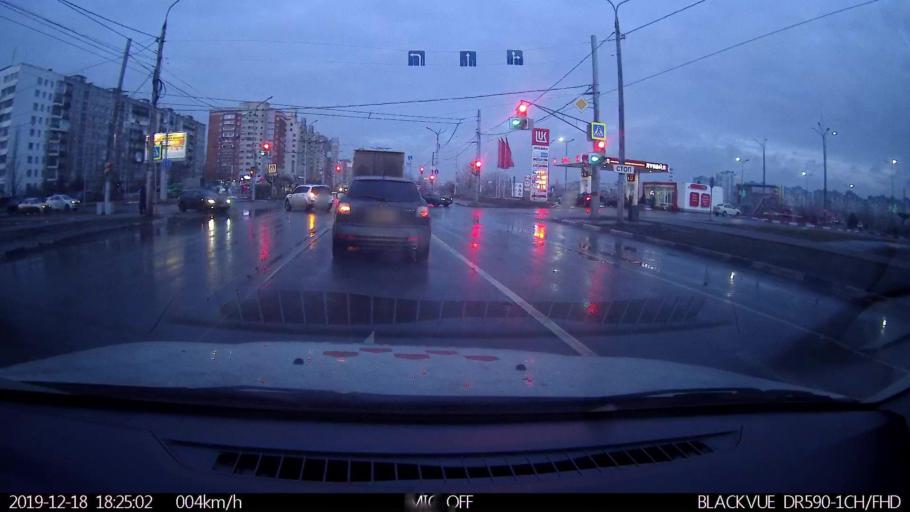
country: RU
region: Nizjnij Novgorod
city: Nizhniy Novgorod
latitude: 56.3329
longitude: 43.9490
